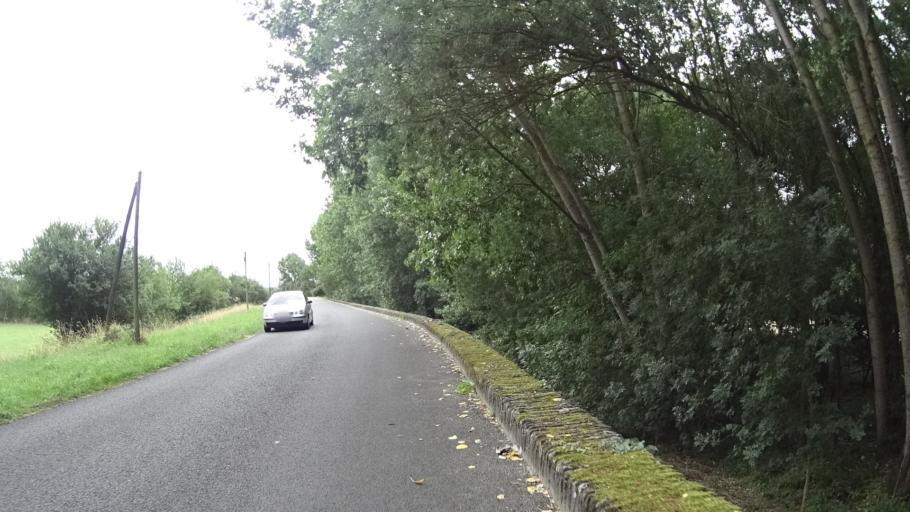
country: FR
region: Pays de la Loire
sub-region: Departement de Maine-et-Loire
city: Les Ponts-de-Ce
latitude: 47.4257
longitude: -0.5126
